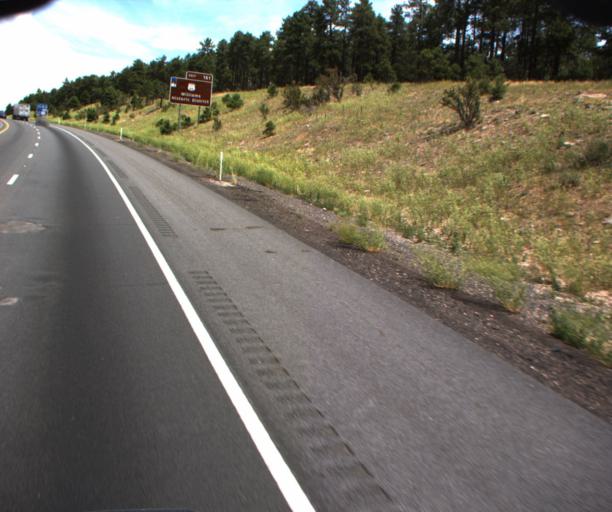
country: US
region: Arizona
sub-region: Coconino County
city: Williams
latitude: 35.2254
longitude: -112.2372
